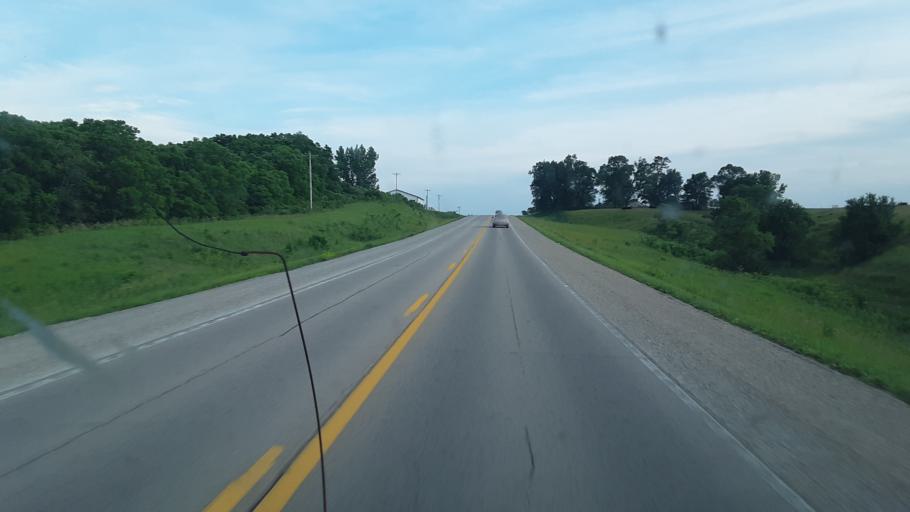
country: US
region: Iowa
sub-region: Benton County
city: Belle Plaine
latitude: 41.8306
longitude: -92.2786
